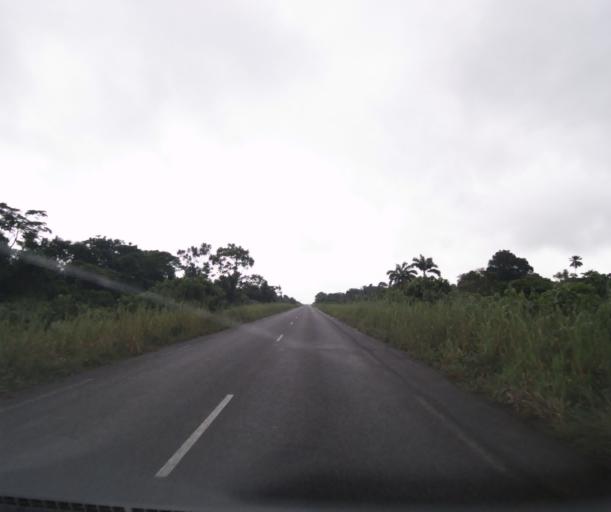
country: CM
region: Littoral
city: Dizangue
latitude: 3.4936
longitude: 10.1203
